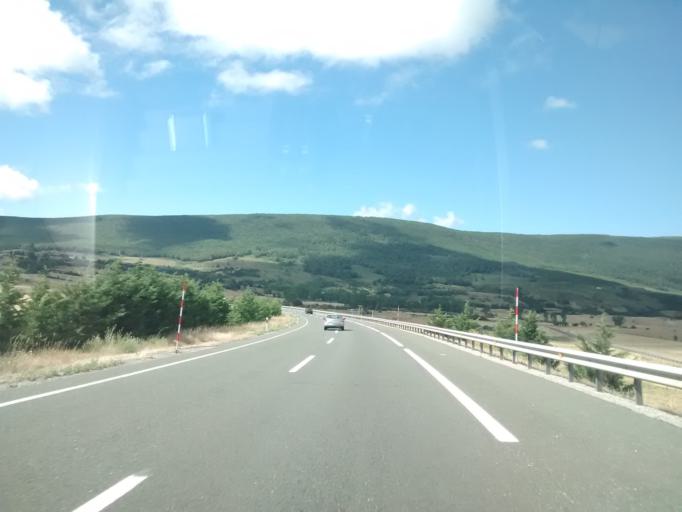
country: ES
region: Cantabria
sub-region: Provincia de Cantabria
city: Villaescusa
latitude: 42.9731
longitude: -4.1565
